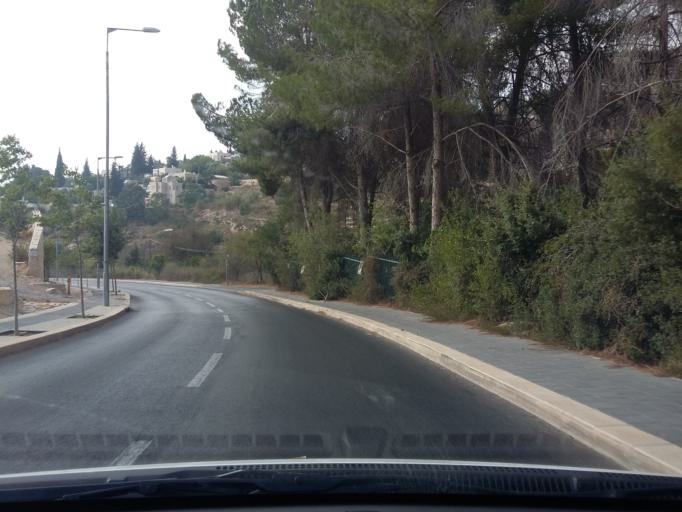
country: IL
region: Jerusalem
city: Jerusalem
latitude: 31.7649
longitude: 35.1693
